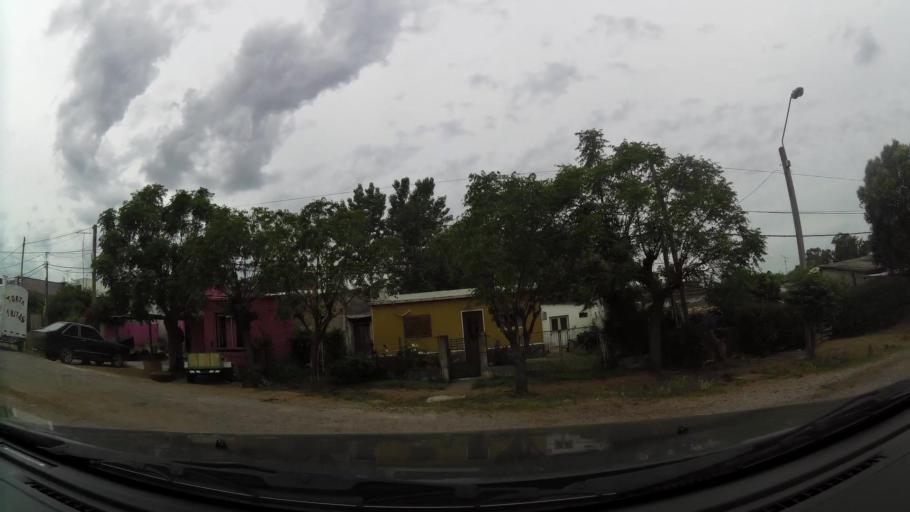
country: UY
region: Canelones
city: Las Piedras
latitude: -34.7105
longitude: -56.2054
